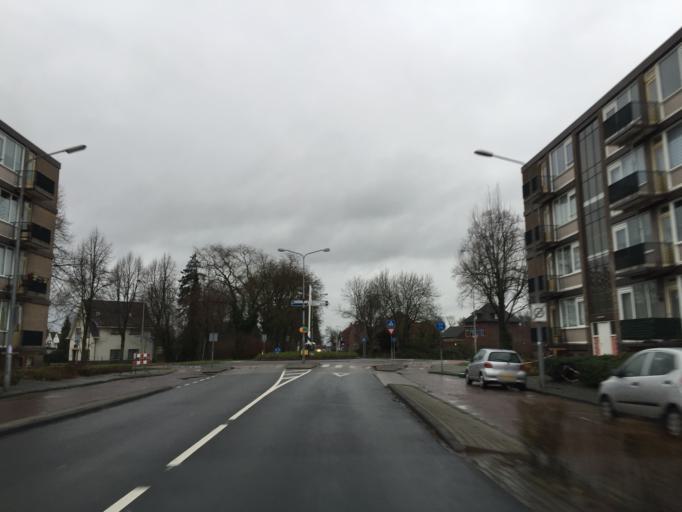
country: NL
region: Limburg
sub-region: Gemeente Maastricht
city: Maastricht
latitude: 50.8624
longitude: 5.6721
